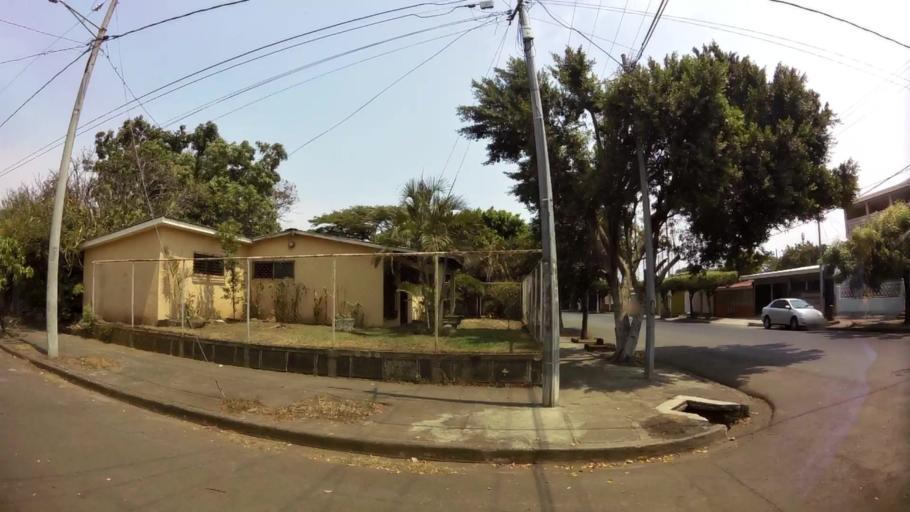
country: NI
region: Managua
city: Ciudad Sandino
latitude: 12.1564
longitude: -86.3131
